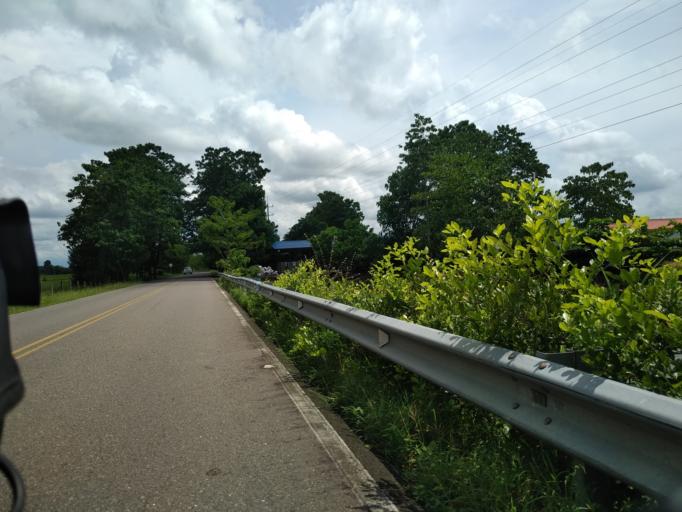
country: CO
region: Santander
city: Puerto Parra
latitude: 6.5085
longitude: -74.0634
